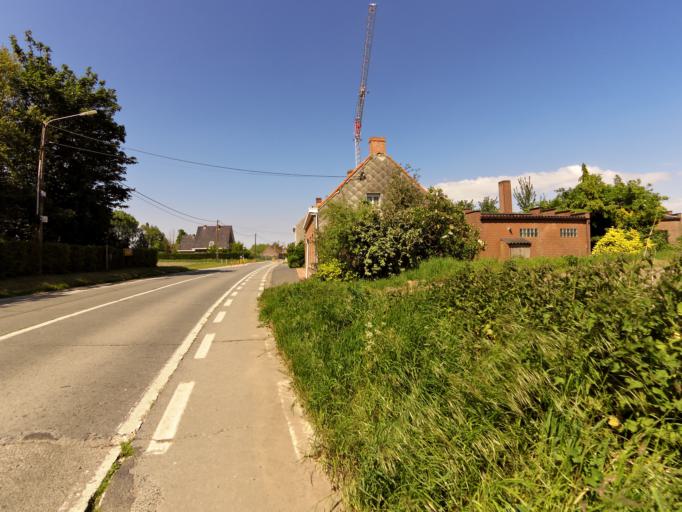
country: BE
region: Flanders
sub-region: Provincie West-Vlaanderen
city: Koekelare
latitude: 51.0514
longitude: 2.9343
